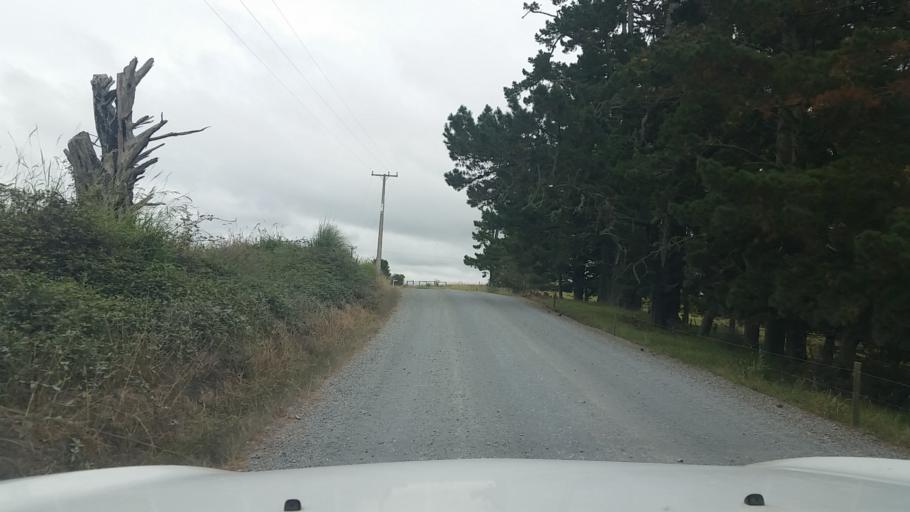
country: NZ
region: Northland
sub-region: Whangarei
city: Maungatapere
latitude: -35.6646
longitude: 174.1796
